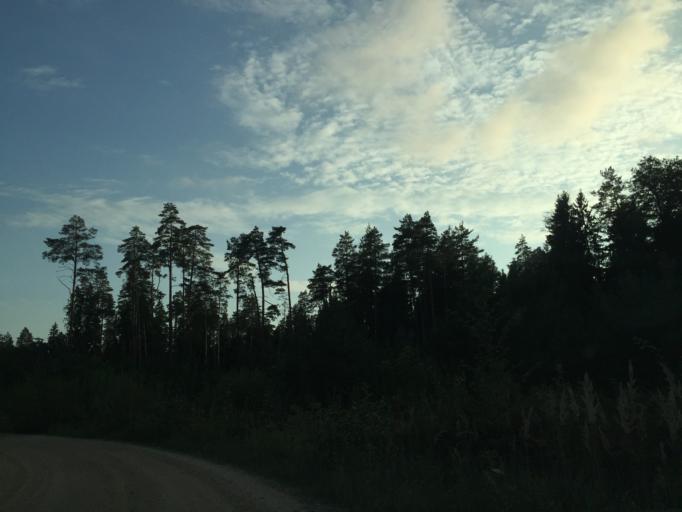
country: LV
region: Baldone
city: Baldone
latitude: 56.7567
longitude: 24.4080
